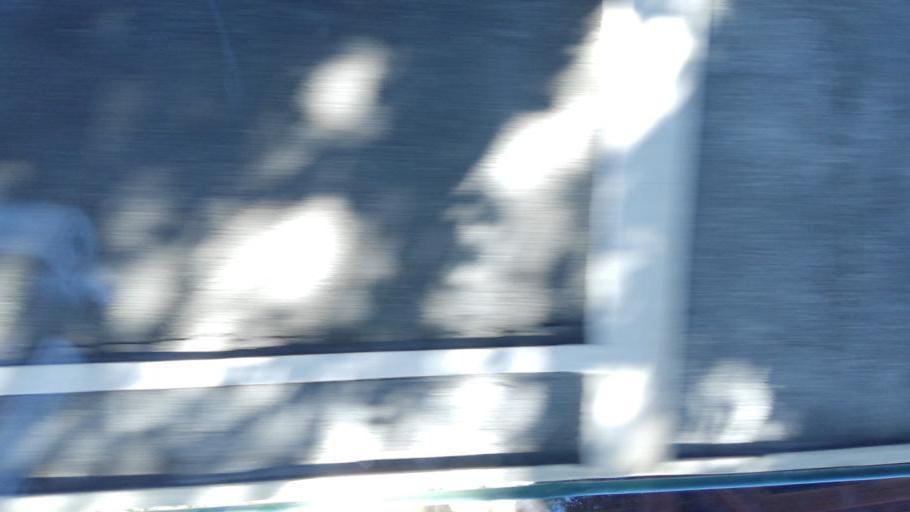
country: MU
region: Plaines Wilhems
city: Ebene
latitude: -20.2317
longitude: 57.4729
